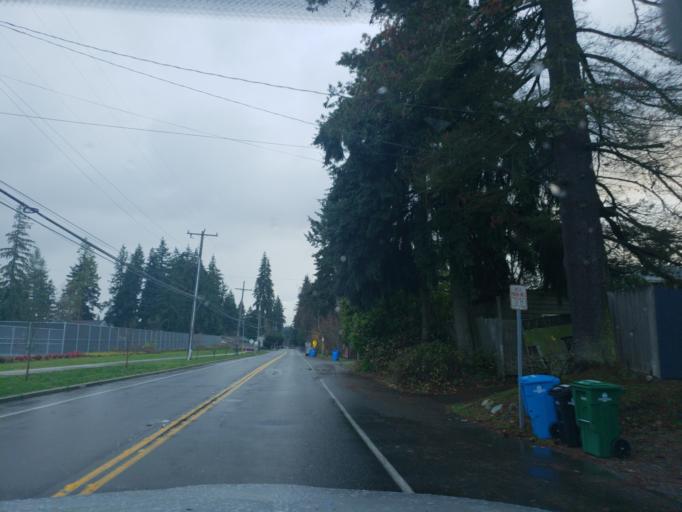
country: US
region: Washington
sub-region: King County
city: Shoreline
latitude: 47.7540
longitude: -122.3510
